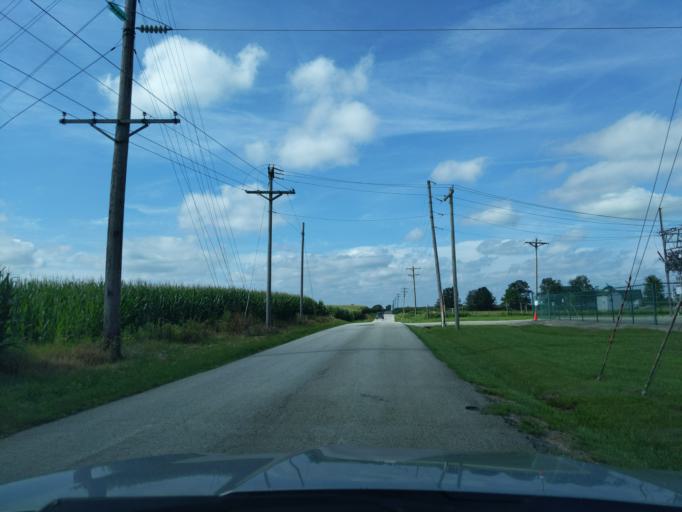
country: US
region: Indiana
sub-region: Ripley County
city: Batesville
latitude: 39.2688
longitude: -85.3475
